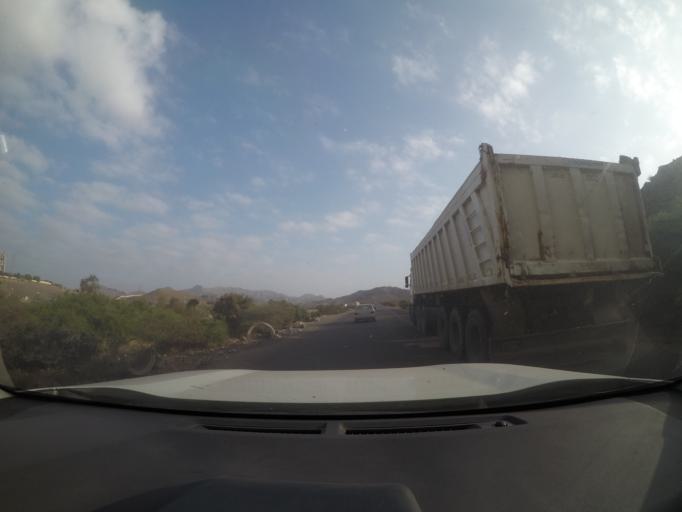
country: YE
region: Lahij
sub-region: Al Milah
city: Al Milah
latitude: 13.3327
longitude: 44.7584
